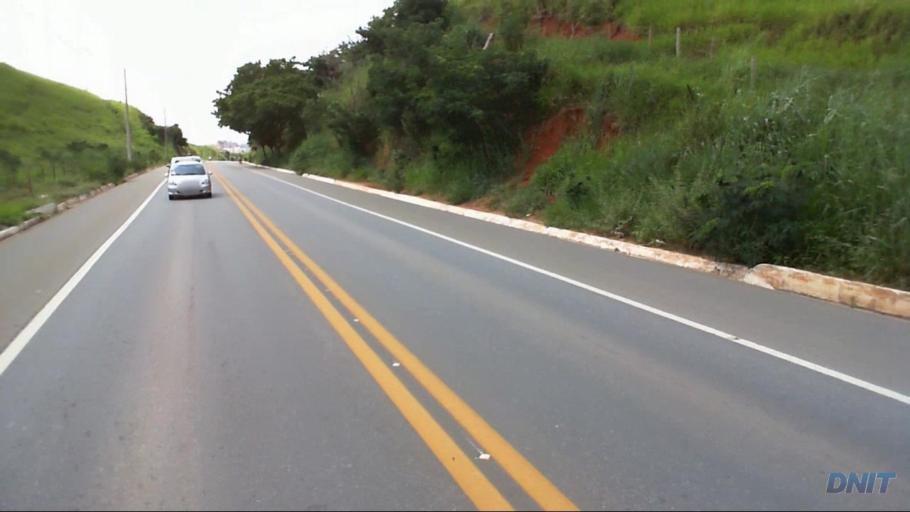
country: BR
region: Minas Gerais
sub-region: Governador Valadares
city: Governador Valadares
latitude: -18.8448
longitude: -41.9744
